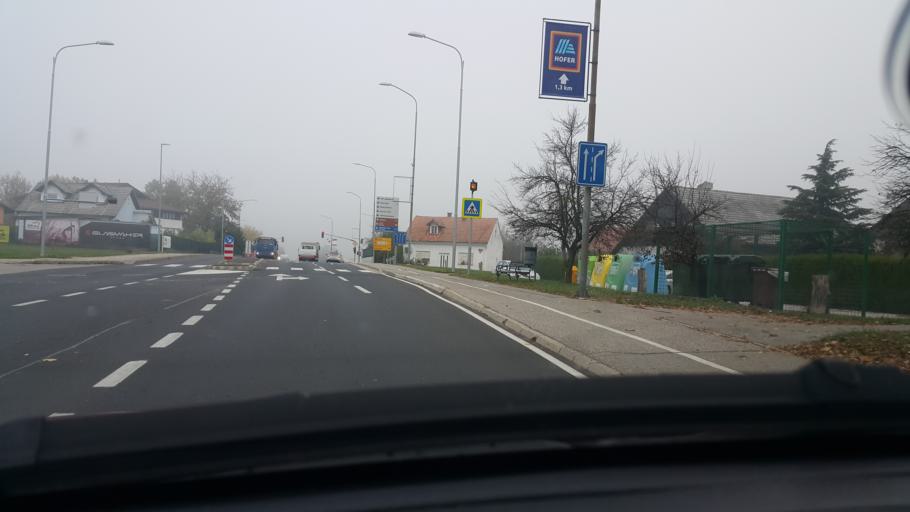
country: SI
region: Brezice
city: Brezice
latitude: 45.9046
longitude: 15.6032
